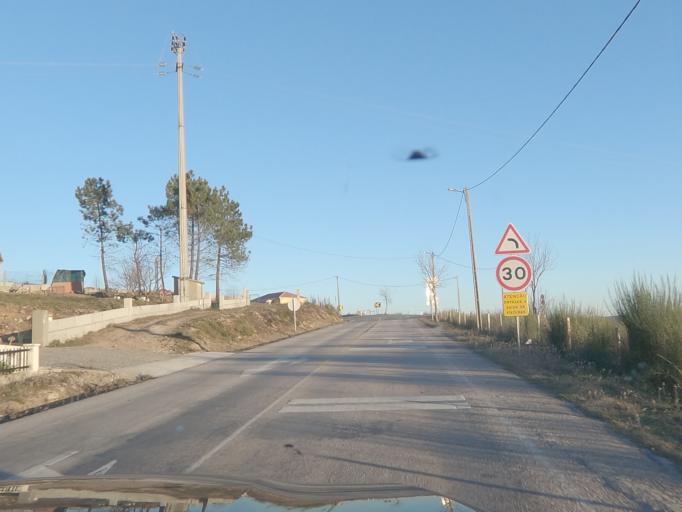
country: PT
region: Vila Real
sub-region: Vila Pouca de Aguiar
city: Vila Pouca de Aguiar
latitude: 41.4952
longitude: -7.7239
